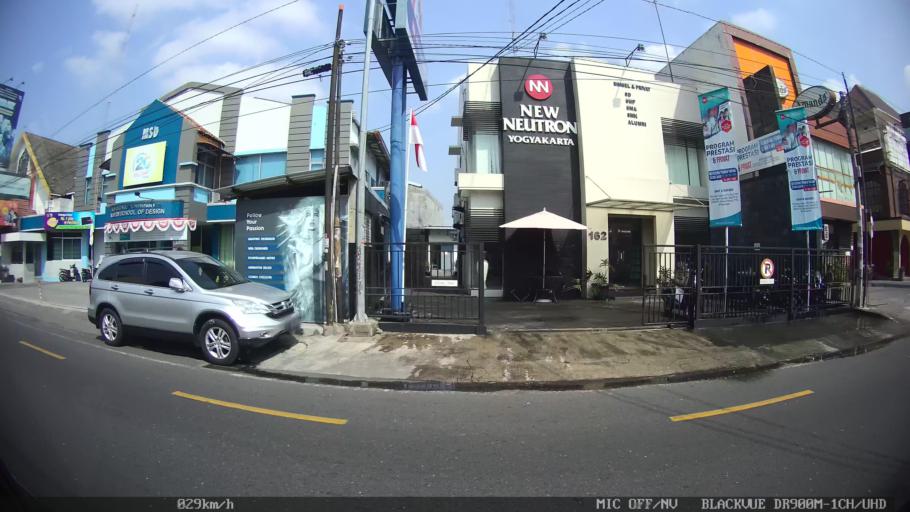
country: ID
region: Daerah Istimewa Yogyakarta
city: Yogyakarta
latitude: -7.8147
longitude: 110.3763
